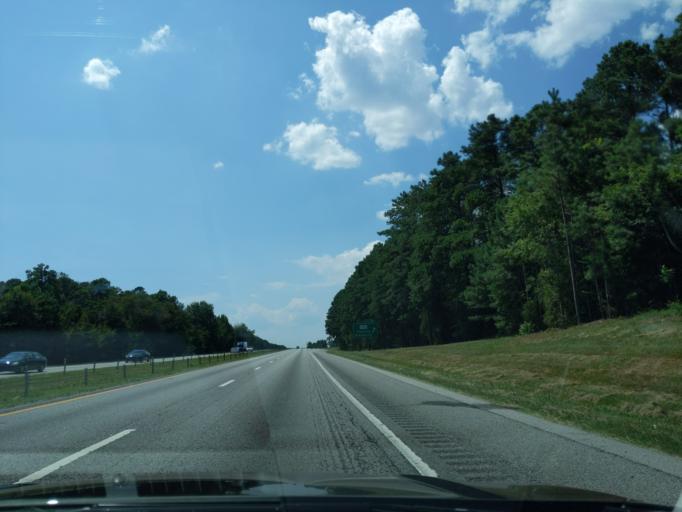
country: US
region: South Carolina
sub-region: Newberry County
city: Prosperity
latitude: 34.2370
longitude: -81.4538
